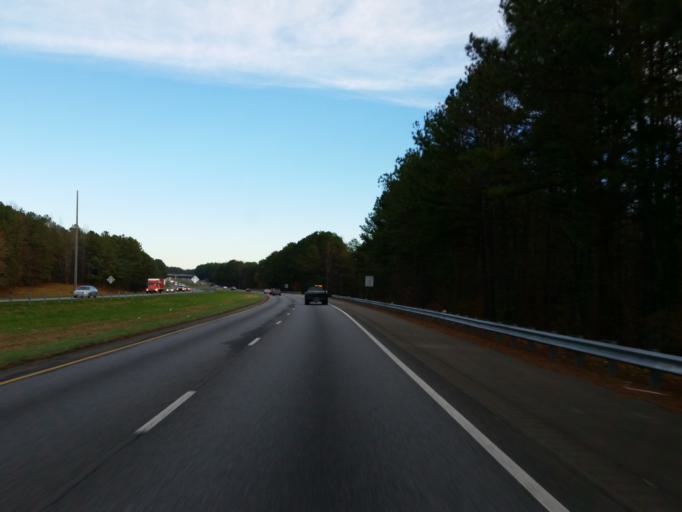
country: US
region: Georgia
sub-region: Cherokee County
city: Holly Springs
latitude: 34.1588
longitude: -84.5111
